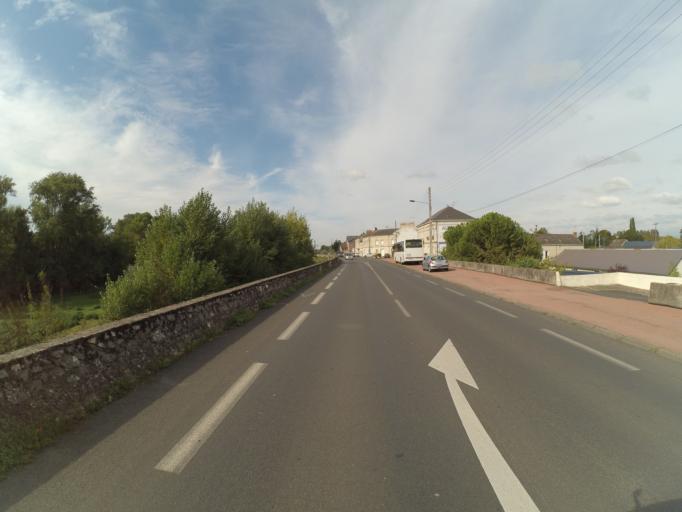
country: FR
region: Pays de la Loire
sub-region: Departement de Maine-et-Loire
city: Villebernier
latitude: 47.2632
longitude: -0.0554
